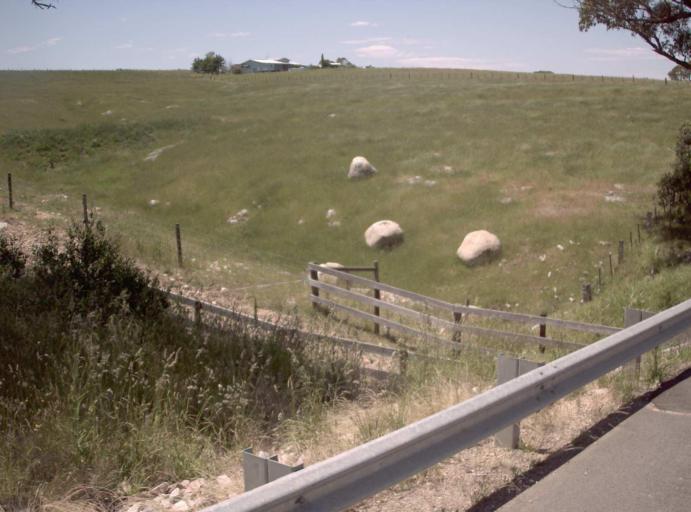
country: AU
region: Victoria
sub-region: East Gippsland
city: Lakes Entrance
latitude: -37.7065
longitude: 148.5012
